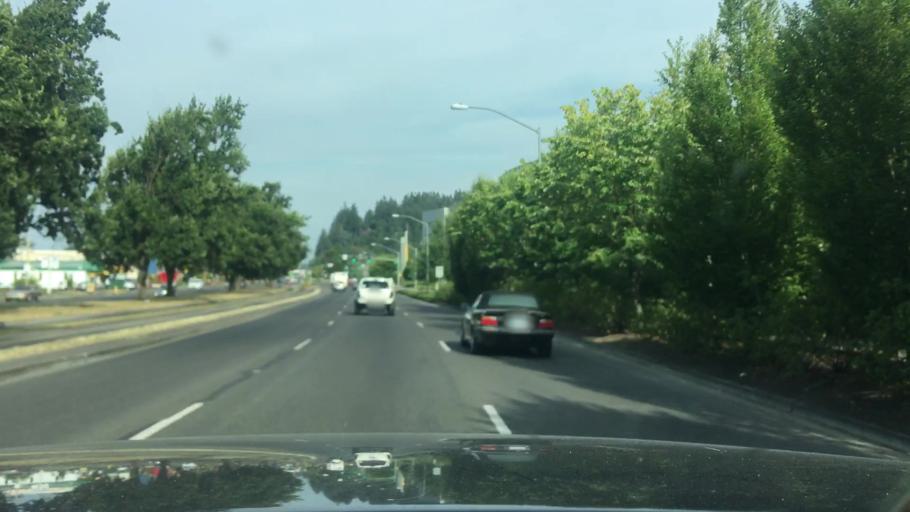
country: US
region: Oregon
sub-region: Lane County
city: Eugene
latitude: 44.0461
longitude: -123.0685
